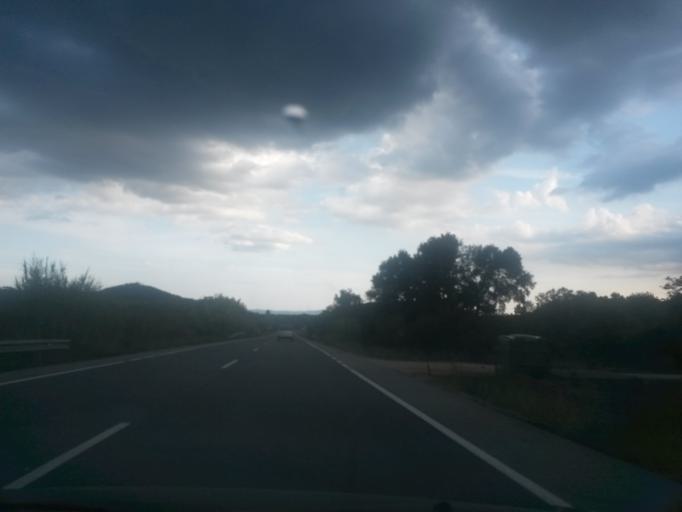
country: ES
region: Catalonia
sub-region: Provincia de Girona
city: Brunyola
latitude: 41.9150
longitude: 2.6575
